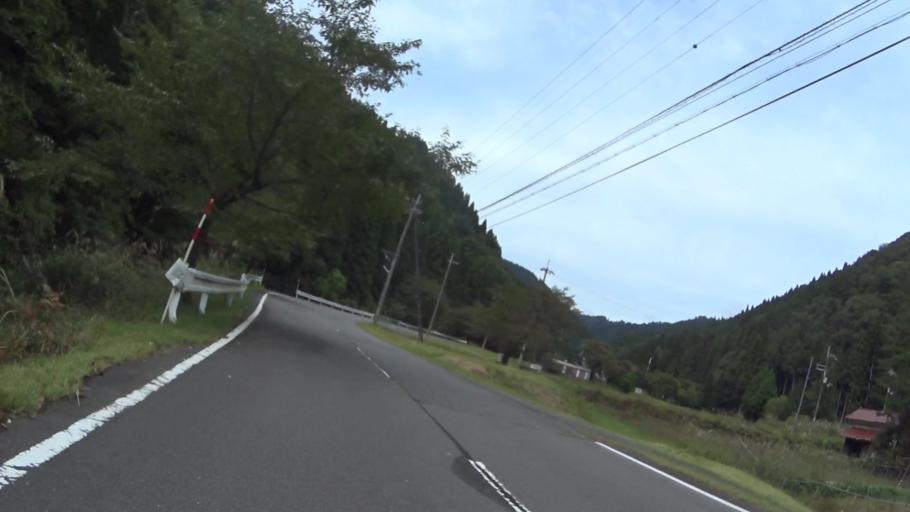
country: JP
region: Shiga Prefecture
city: Kitahama
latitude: 35.2633
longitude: 135.7483
